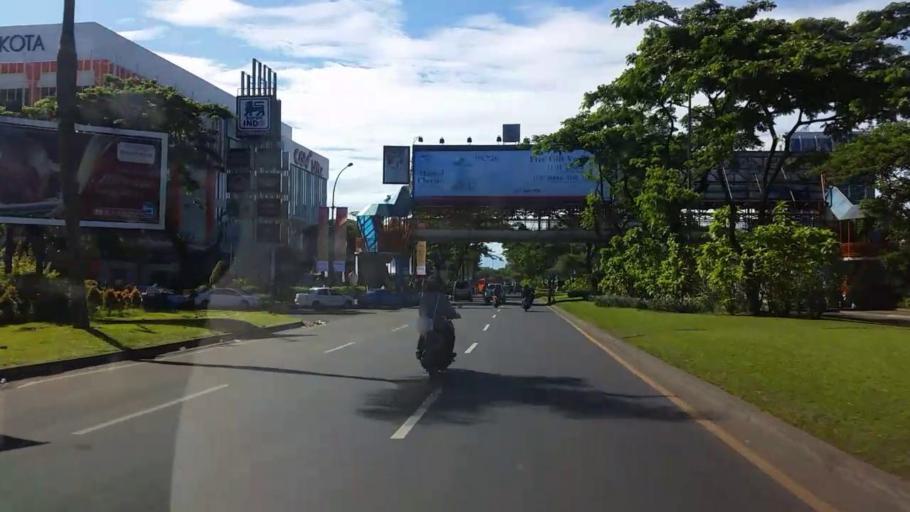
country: ID
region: West Java
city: Serpong
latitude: -6.2946
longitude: 106.6664
